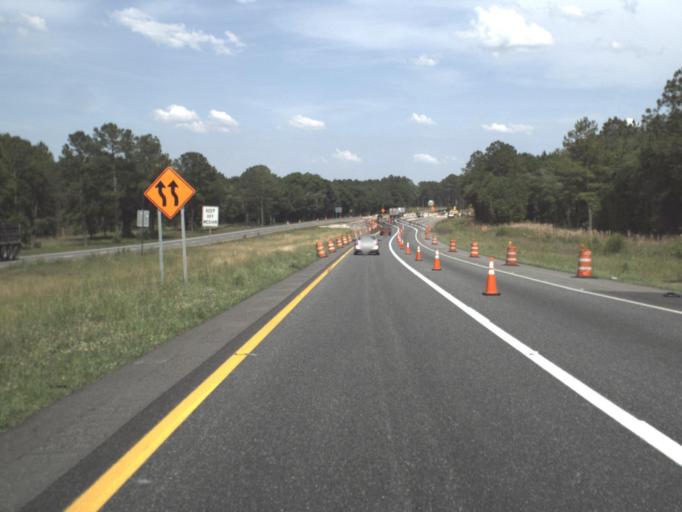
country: US
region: Florida
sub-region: Columbia County
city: Five Points
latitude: 30.2451
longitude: -82.6704
